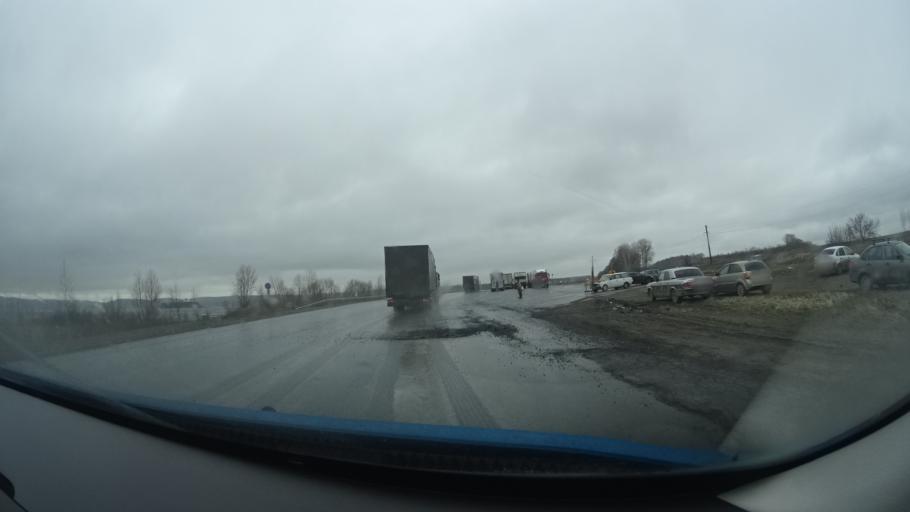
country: RU
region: Bashkortostan
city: Kandry
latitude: 54.5193
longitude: 54.0535
